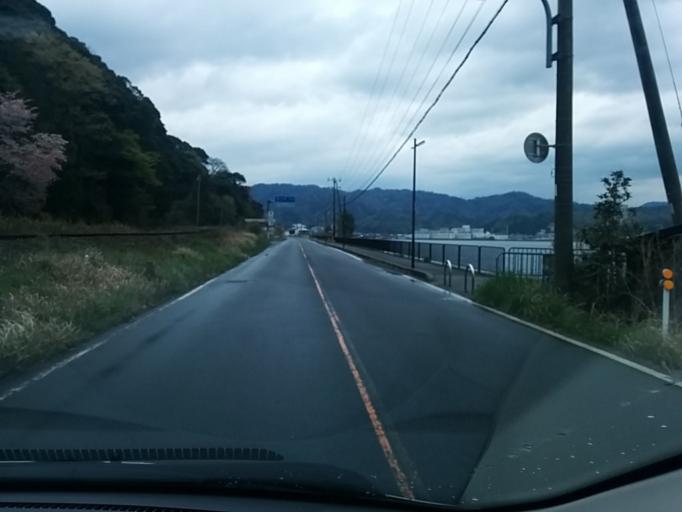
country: JP
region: Kyoto
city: Miyazu
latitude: 35.5618
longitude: 135.1738
